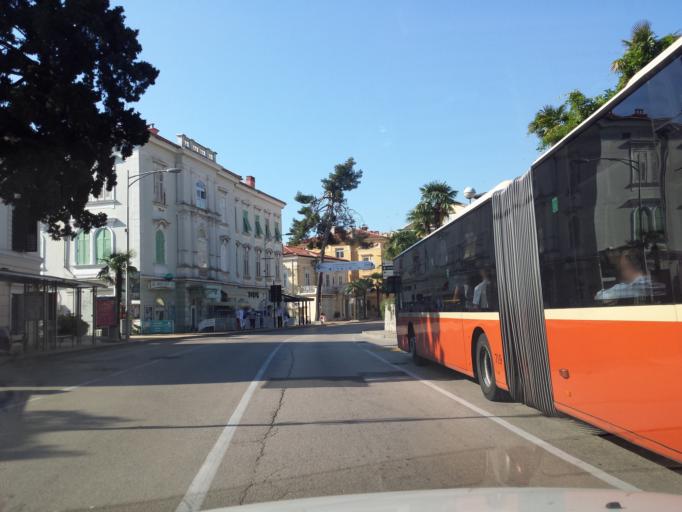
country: HR
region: Primorsko-Goranska
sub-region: Grad Opatija
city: Opatija
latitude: 45.3394
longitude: 14.3098
